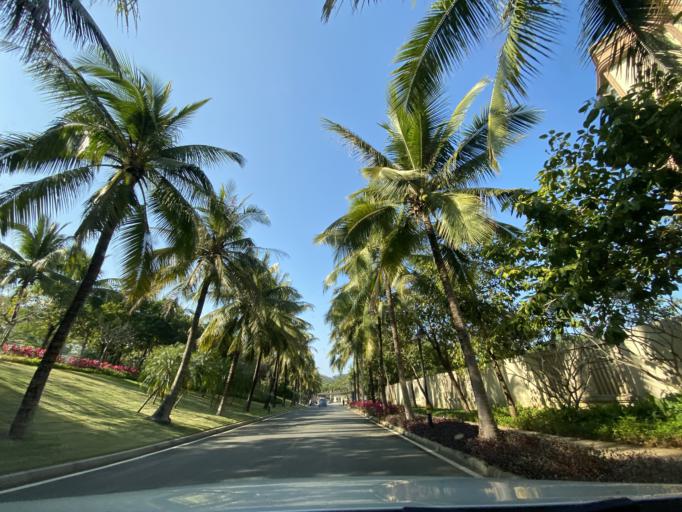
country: CN
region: Hainan
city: Yingzhou
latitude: 18.4177
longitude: 109.8964
